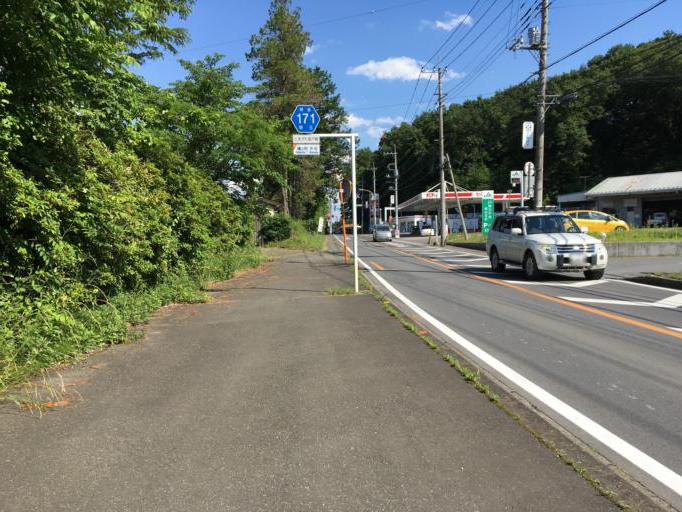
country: JP
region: Saitama
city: Morohongo
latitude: 35.9841
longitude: 139.3328
